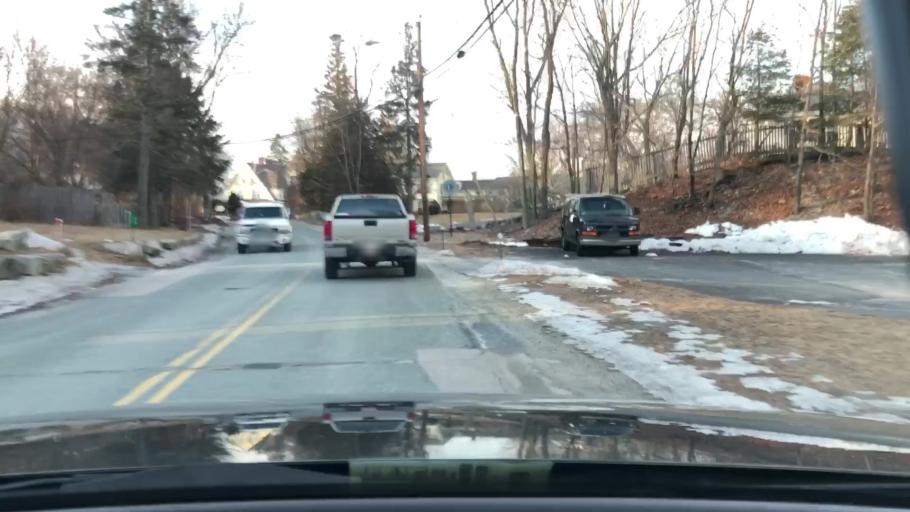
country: US
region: Massachusetts
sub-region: Worcester County
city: Millville
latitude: 42.0208
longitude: -71.5829
